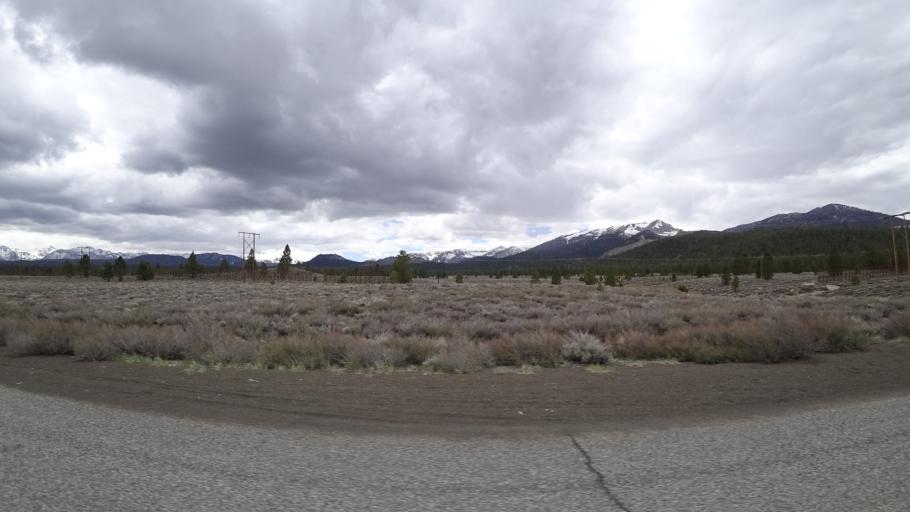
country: US
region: California
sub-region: Mono County
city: Mammoth Lakes
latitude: 37.7477
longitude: -118.9817
